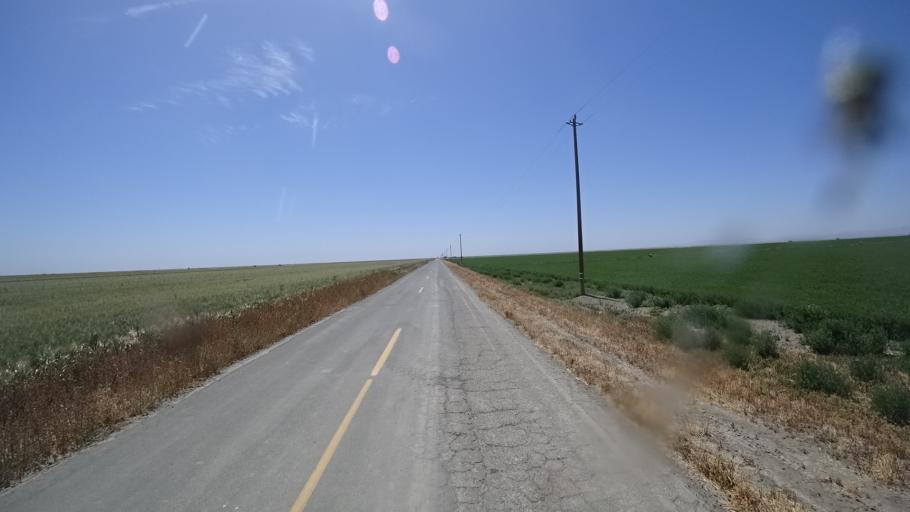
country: US
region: California
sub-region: Kings County
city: Stratford
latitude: 36.1348
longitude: -119.7340
